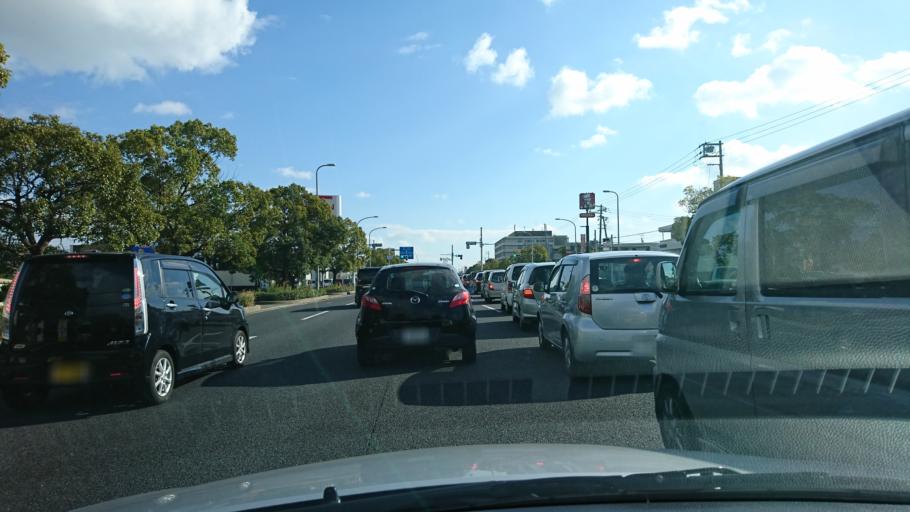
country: JP
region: Hyogo
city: Kakogawacho-honmachi
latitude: 34.7375
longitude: 134.8495
